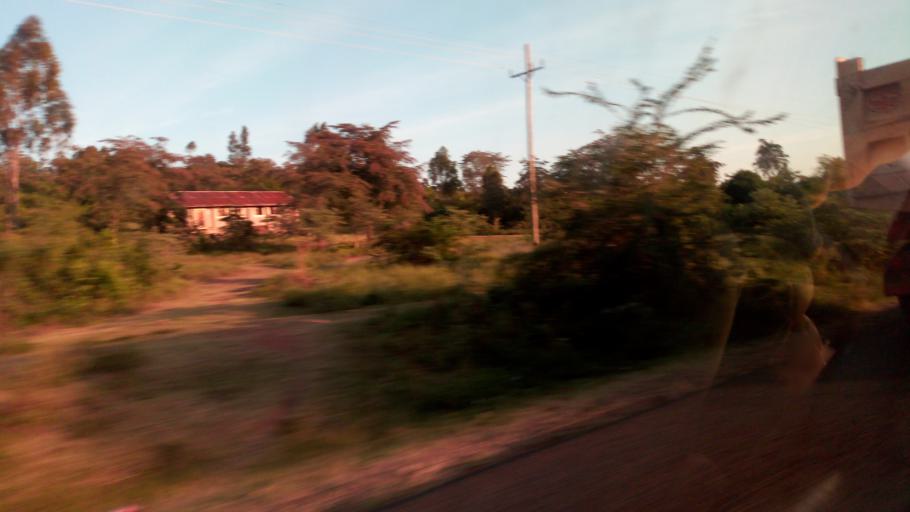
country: KE
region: Kisumu
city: Ahero
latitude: -0.3472
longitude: 35.0034
